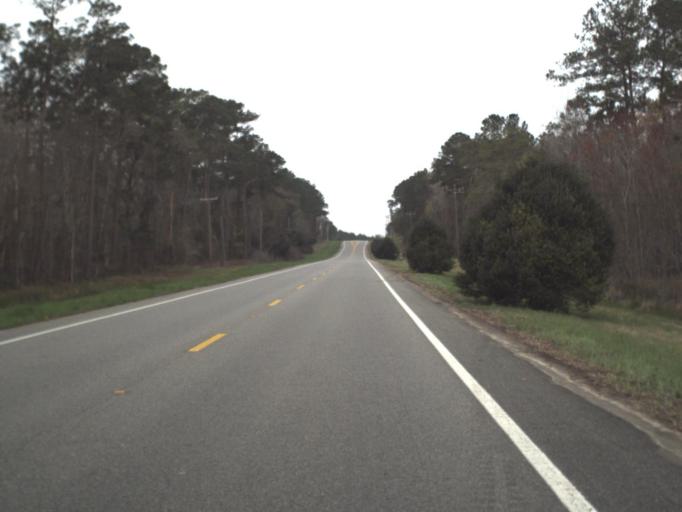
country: US
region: Florida
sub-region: Jefferson County
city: Monticello
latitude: 30.5205
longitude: -83.7878
